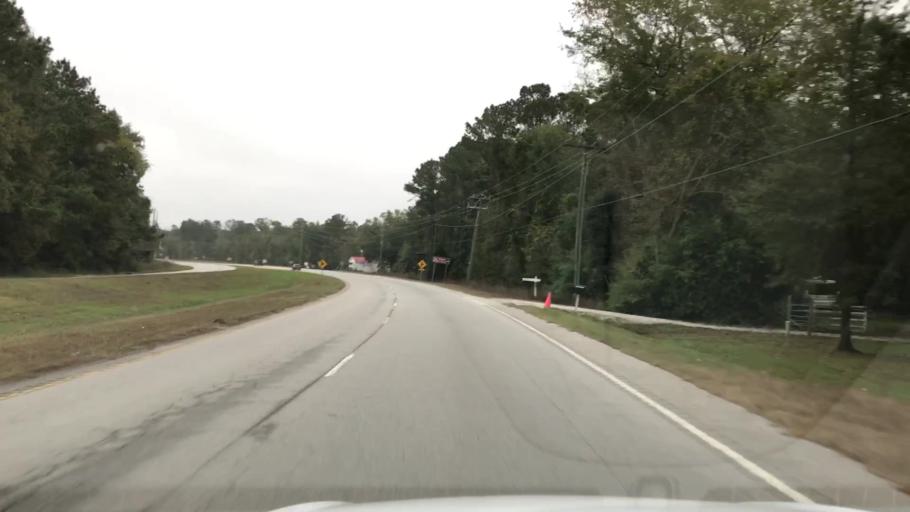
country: US
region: South Carolina
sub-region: Charleston County
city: Awendaw
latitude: 32.9884
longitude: -79.6472
